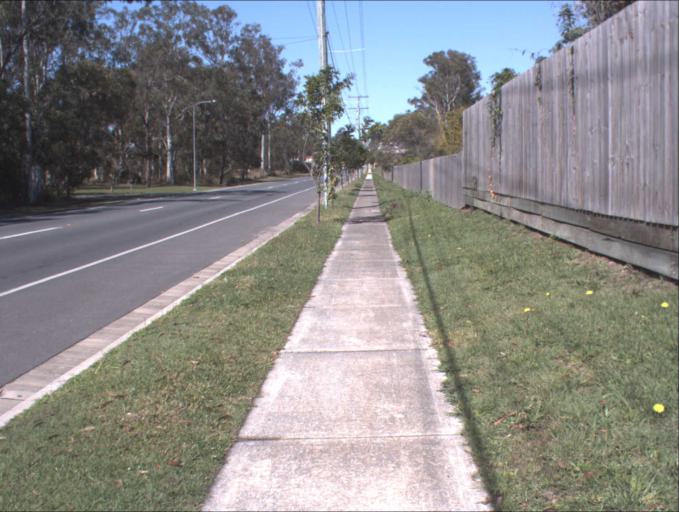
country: AU
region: Queensland
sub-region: Logan
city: Logan City
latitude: -27.6701
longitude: 153.0950
